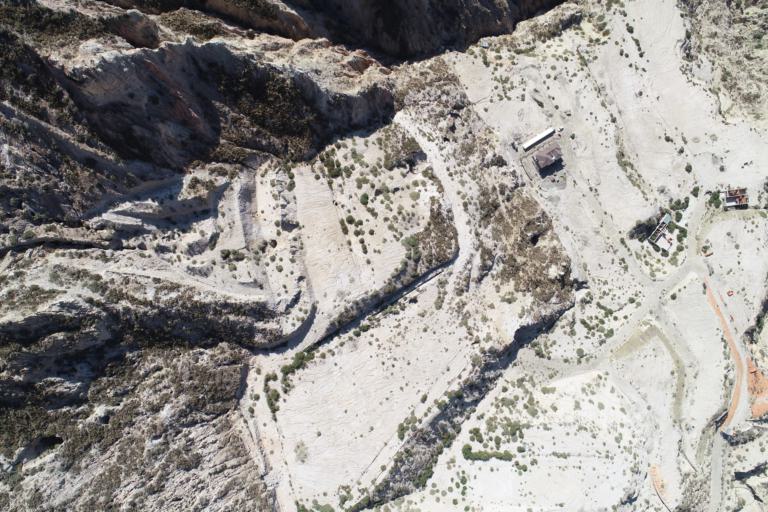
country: BO
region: La Paz
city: La Paz
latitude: -16.5545
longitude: -68.1073
